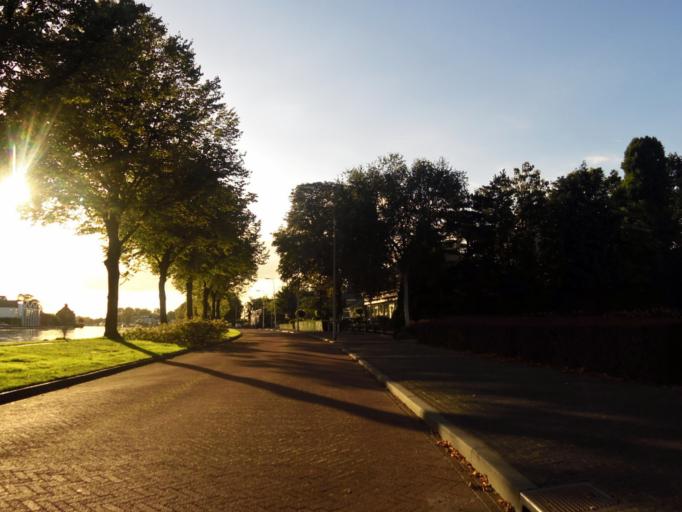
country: NL
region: South Holland
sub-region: Gemeente Alphen aan den Rijn
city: Alphen aan den Rijn
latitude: 52.1428
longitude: 4.6539
